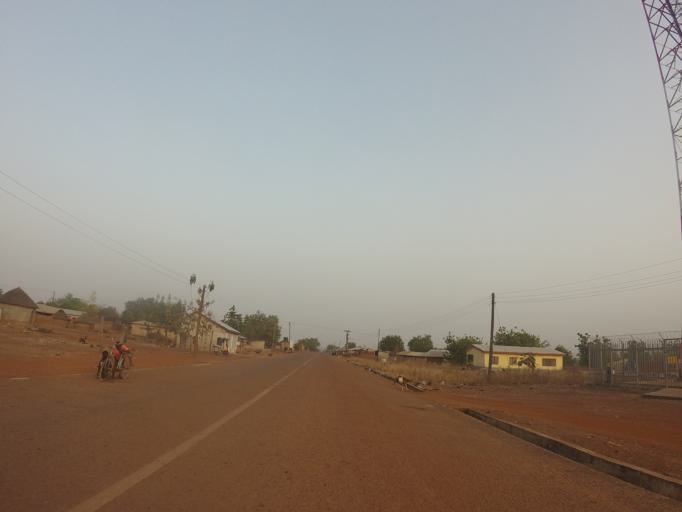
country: GH
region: Northern
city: Tamale
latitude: 9.4456
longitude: -1.1180
